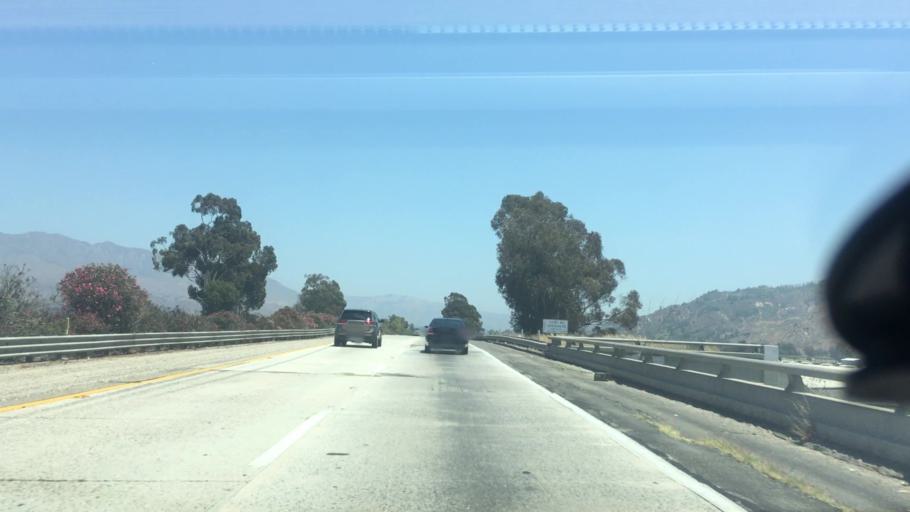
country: US
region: California
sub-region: Ventura County
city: Saticoy
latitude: 34.3141
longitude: -119.1151
